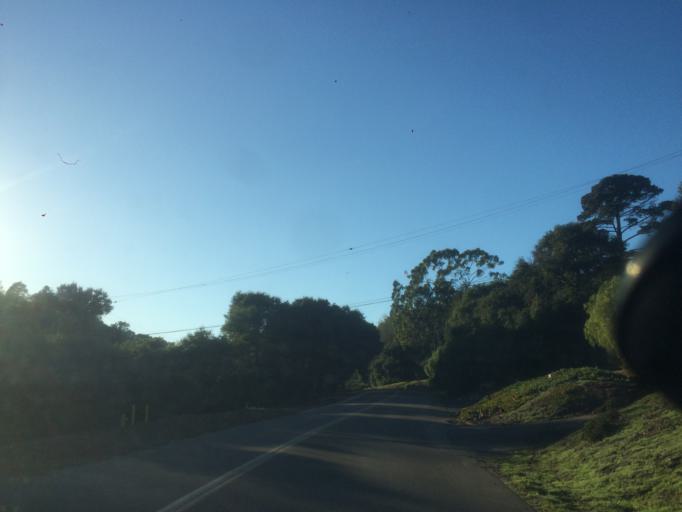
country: US
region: California
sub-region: Santa Barbara County
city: Goleta
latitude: 34.4215
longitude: -119.7677
